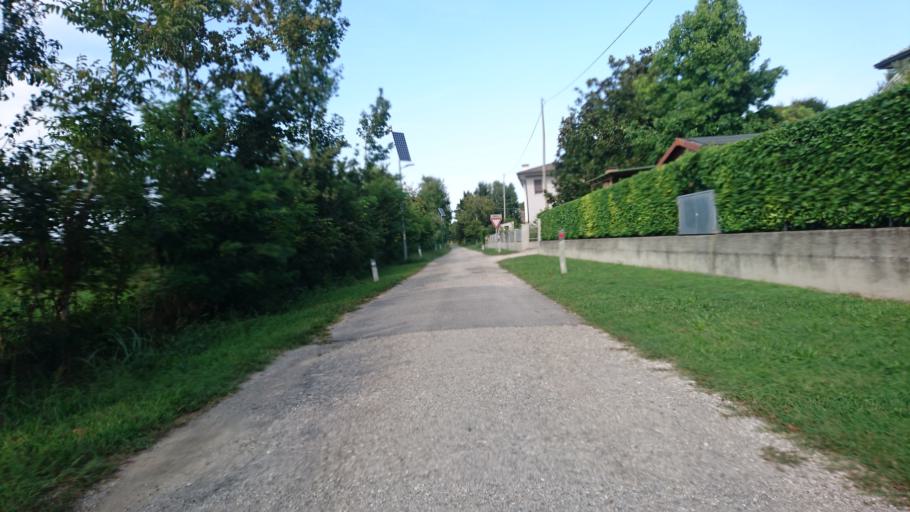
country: IT
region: Veneto
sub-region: Provincia di Padova
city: Selvazzano Dentro
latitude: 45.4000
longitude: 11.7858
